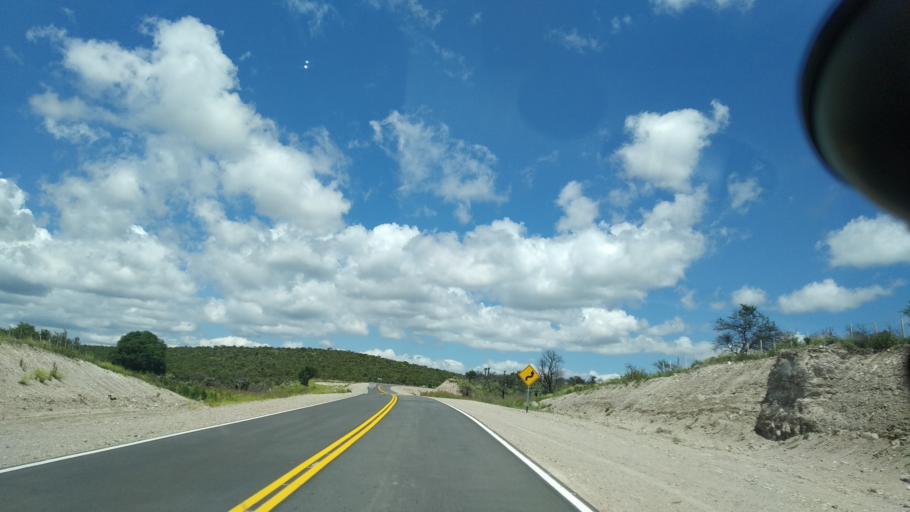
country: AR
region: Cordoba
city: Salsacate
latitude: -31.3737
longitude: -65.2741
